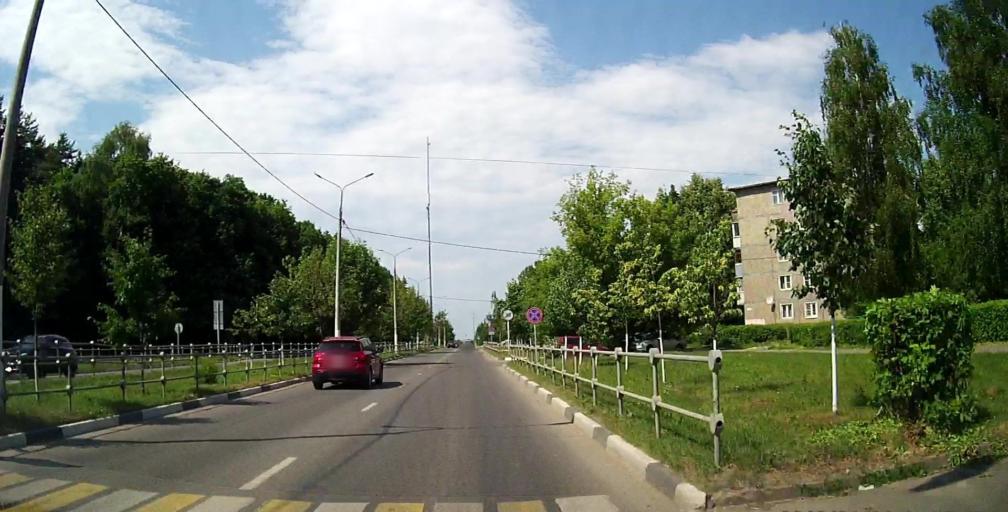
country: RU
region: Moskovskaya
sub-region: Podol'skiy Rayon
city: Podol'sk
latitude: 55.4147
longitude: 37.5218
